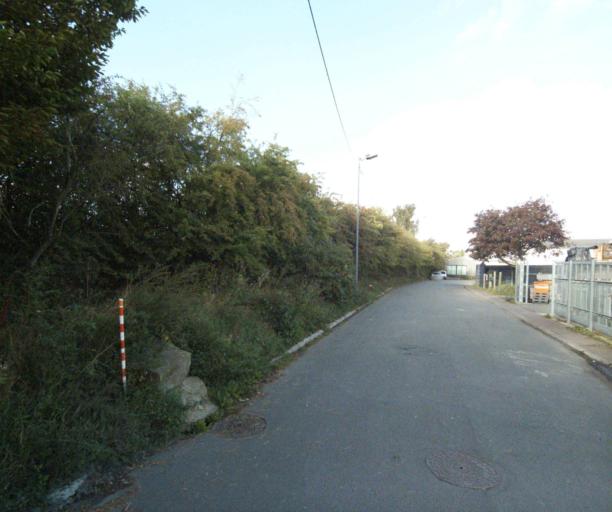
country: FR
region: Nord-Pas-de-Calais
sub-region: Departement du Nord
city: Sequedin
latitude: 50.6297
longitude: 2.9954
